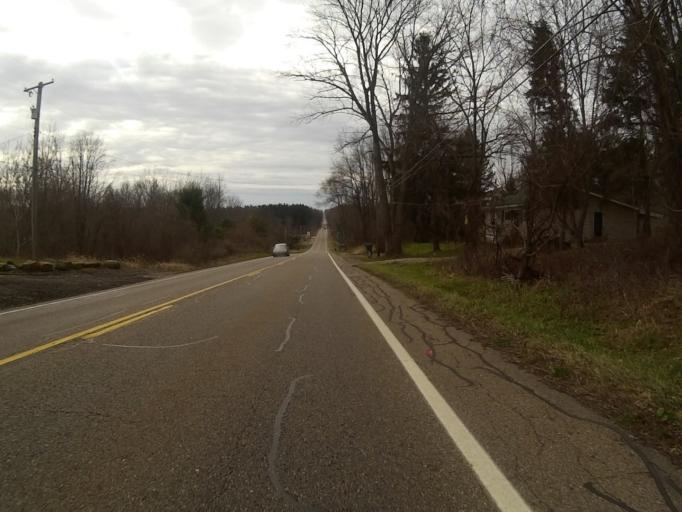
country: US
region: Ohio
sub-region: Portage County
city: Brimfield
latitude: 41.0635
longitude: -81.3472
